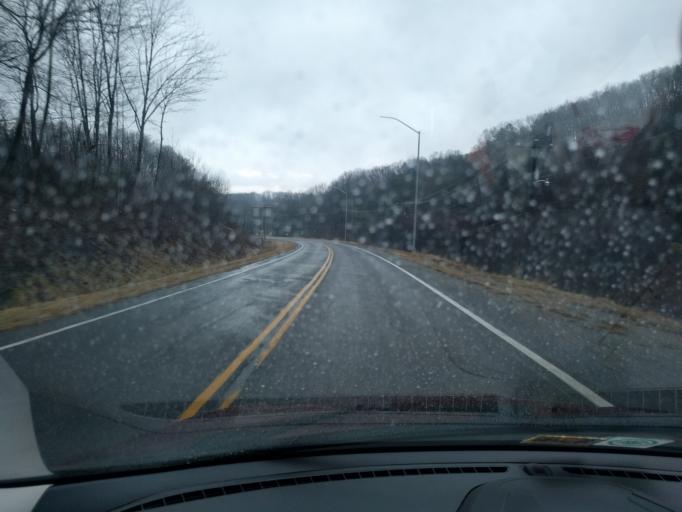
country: US
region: Virginia
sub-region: Pulaski County
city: Pulaski
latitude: 37.0397
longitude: -80.7379
